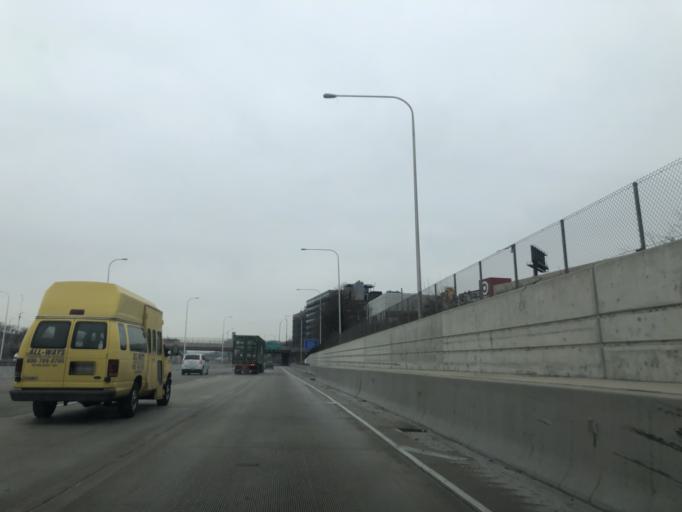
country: US
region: Illinois
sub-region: Cook County
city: Chicago
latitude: 41.8762
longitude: -87.6538
